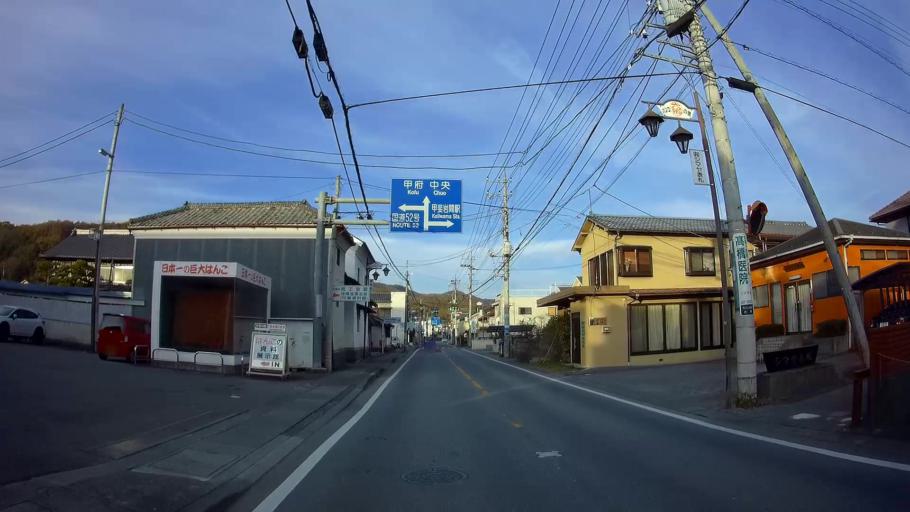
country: JP
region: Yamanashi
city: Ryuo
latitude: 35.4922
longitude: 138.4602
